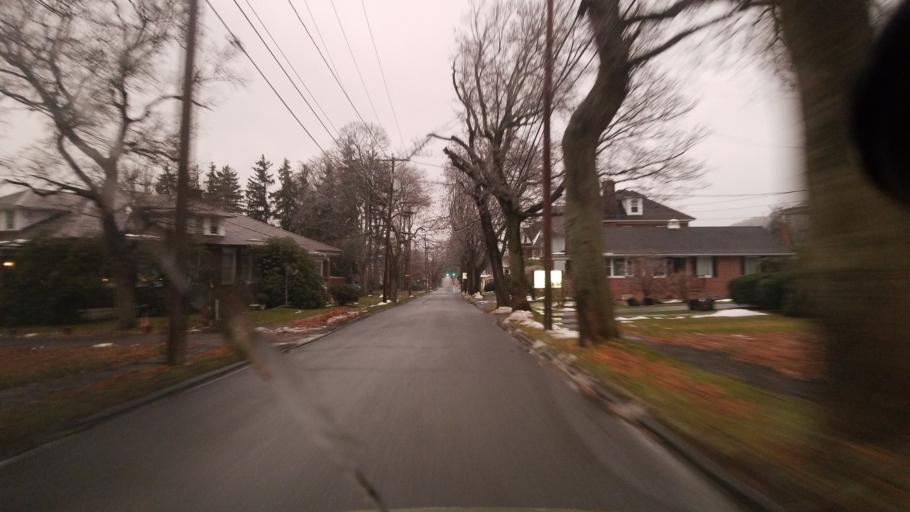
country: US
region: Pennsylvania
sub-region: Clearfield County
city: Clearfield
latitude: 41.0297
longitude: -78.4489
